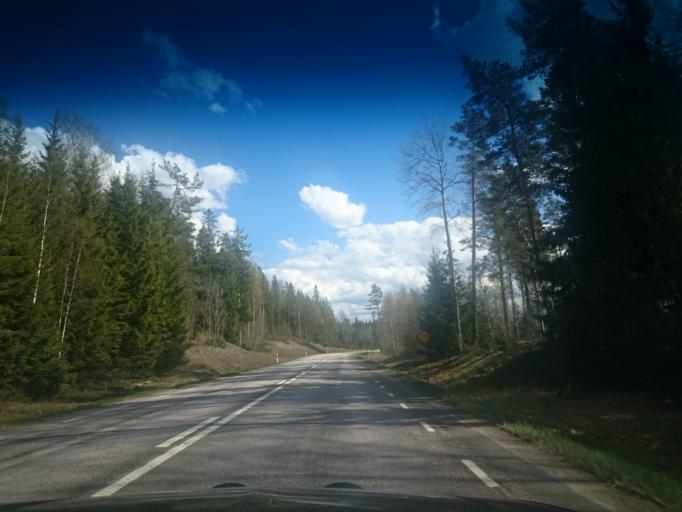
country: SE
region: Kronoberg
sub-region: Vaxjo Kommun
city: Braas
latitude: 57.2359
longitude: 15.1458
